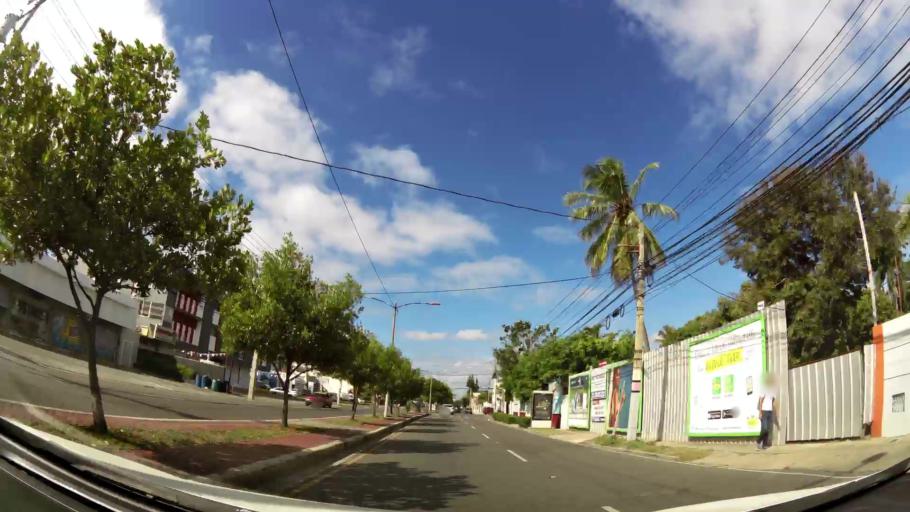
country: DO
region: Nacional
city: Bella Vista
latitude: 18.4573
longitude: -69.9400
